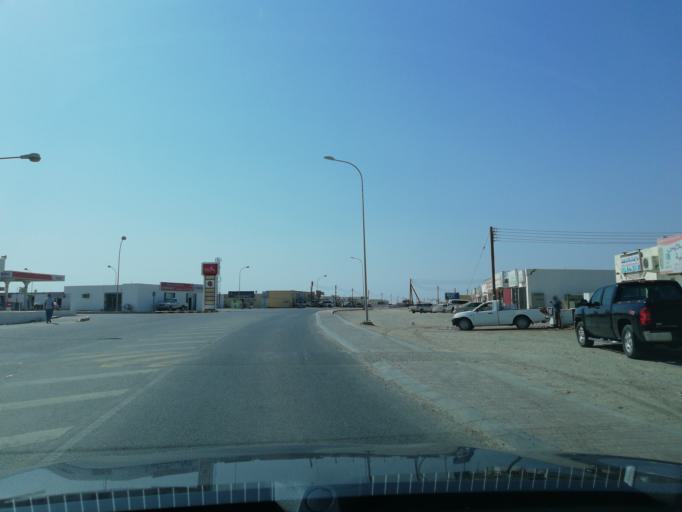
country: OM
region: Muhafazat ad Dakhiliyah
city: Adam
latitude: 22.3000
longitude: 58.0741
